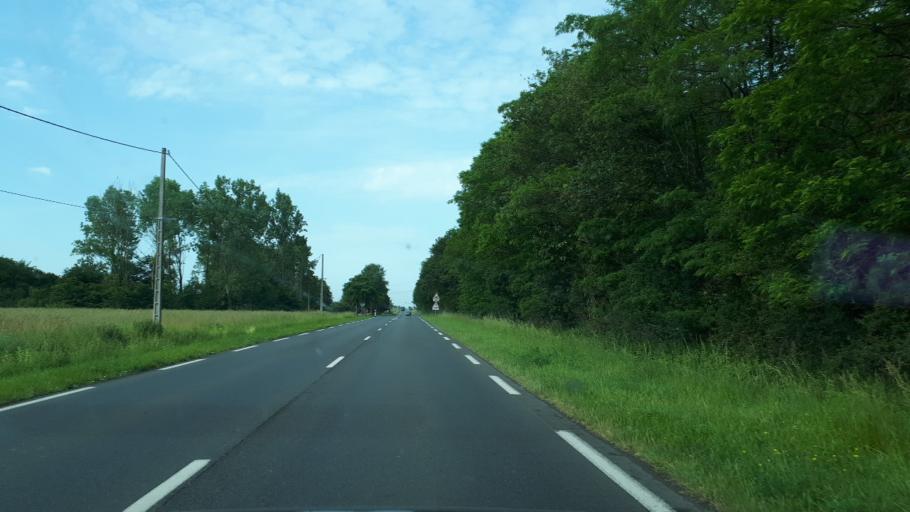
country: FR
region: Centre
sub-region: Departement d'Indre-et-Loire
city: Monnaie
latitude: 47.4858
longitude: 0.7701
